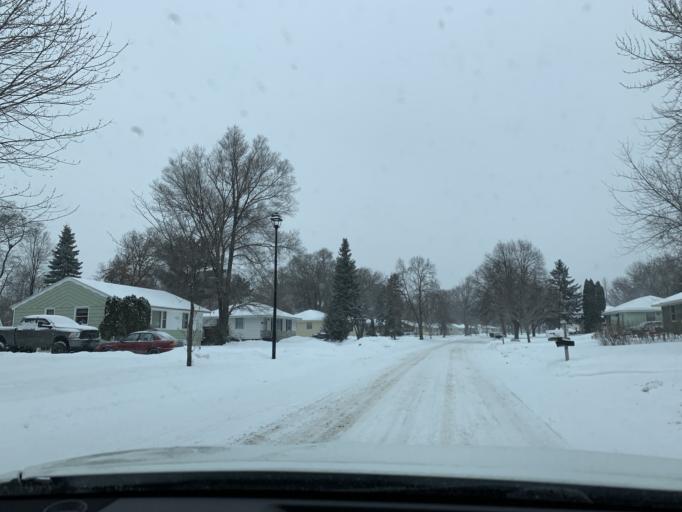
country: US
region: Minnesota
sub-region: Anoka County
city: Blaine
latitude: 45.1756
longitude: -93.2868
